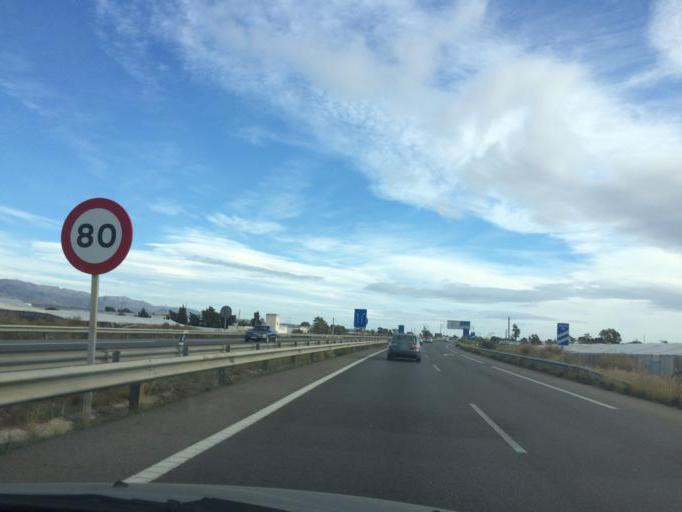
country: ES
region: Andalusia
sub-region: Provincia de Almeria
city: Viator
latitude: 36.8484
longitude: -2.3850
